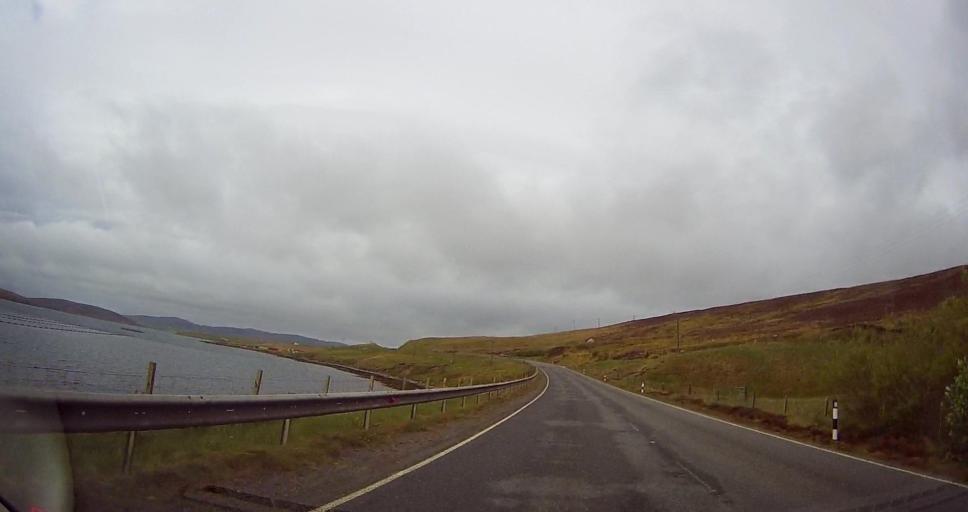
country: GB
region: Scotland
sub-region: Shetland Islands
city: Lerwick
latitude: 60.3694
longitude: -1.2996
